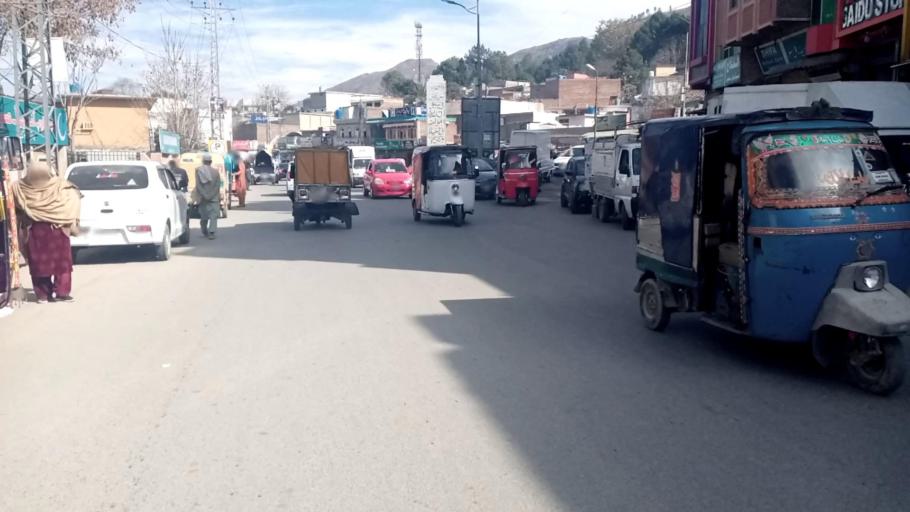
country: PK
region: Khyber Pakhtunkhwa
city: Saidu Sharif
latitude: 34.7490
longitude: 72.3568
